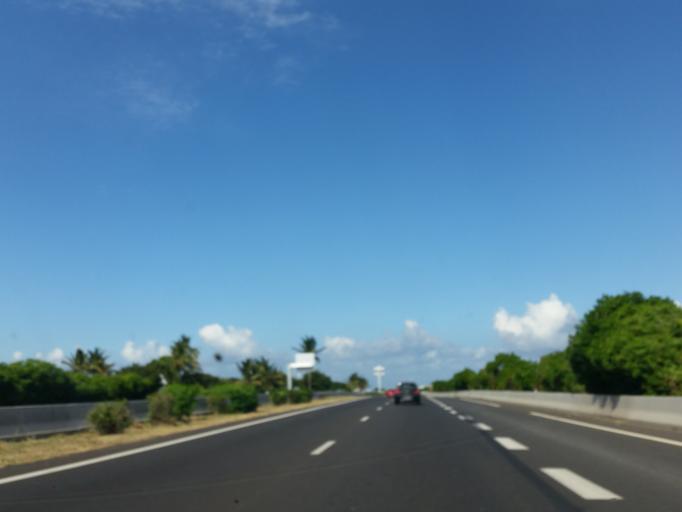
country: RE
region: Reunion
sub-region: Reunion
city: Saint-Louis
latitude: -21.3055
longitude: 55.4289
